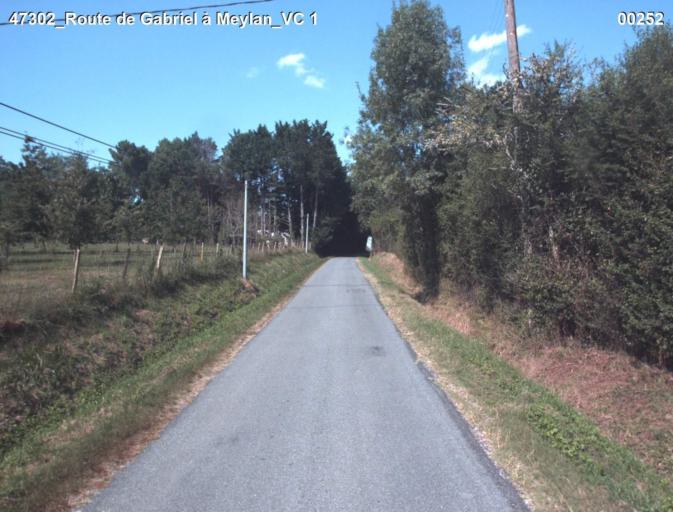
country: FR
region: Aquitaine
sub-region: Departement du Lot-et-Garonne
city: Mezin
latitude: 44.0538
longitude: 0.1422
